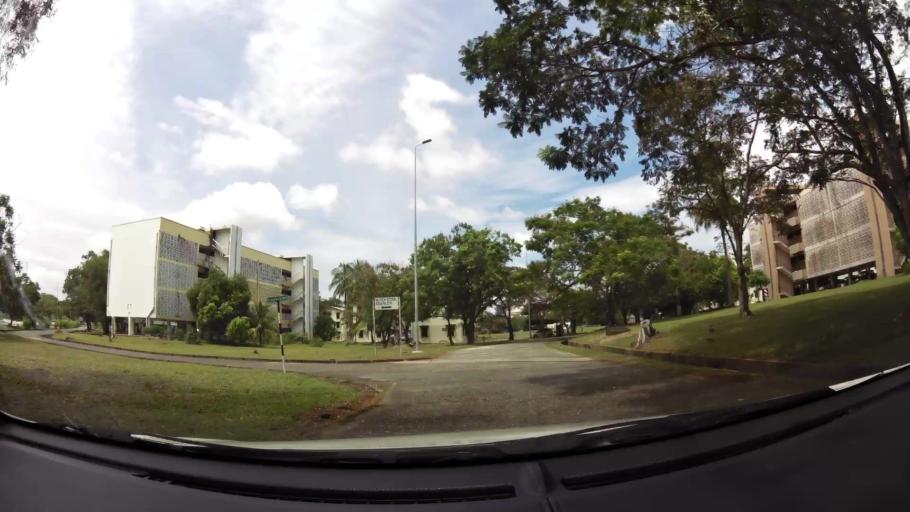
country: BN
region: Brunei and Muara
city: Bandar Seri Begawan
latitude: 4.9206
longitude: 114.9312
